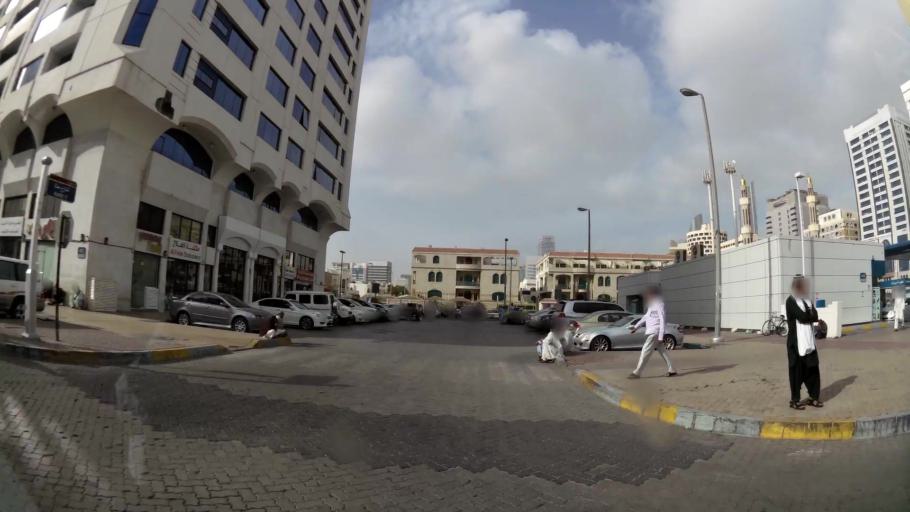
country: AE
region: Abu Dhabi
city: Abu Dhabi
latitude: 24.4880
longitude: 54.3708
